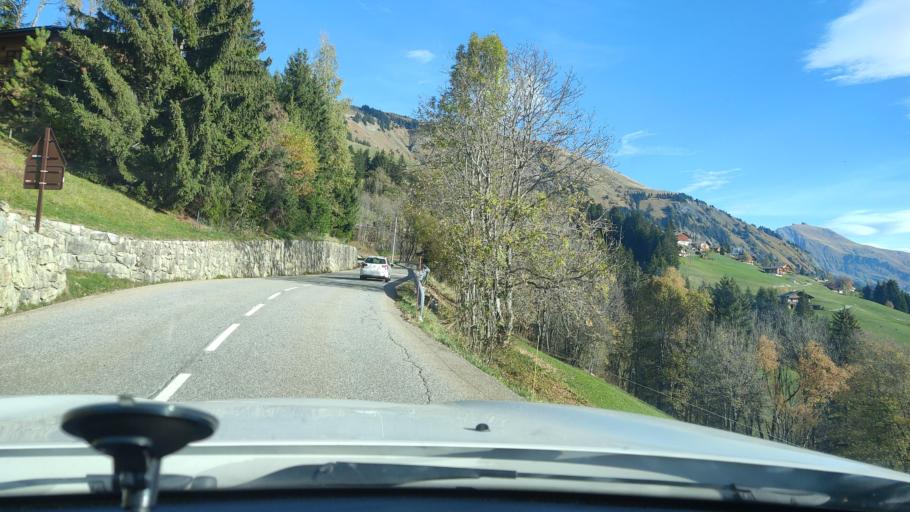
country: FR
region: Rhone-Alpes
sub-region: Departement de la Savoie
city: Beaufort
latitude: 45.7494
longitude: 6.5763
